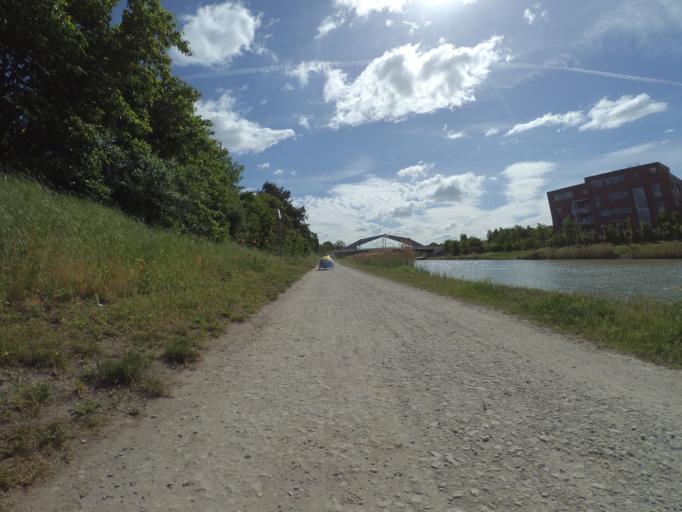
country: DE
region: Lower Saxony
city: Langenhagen
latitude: 52.4067
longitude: 9.7885
